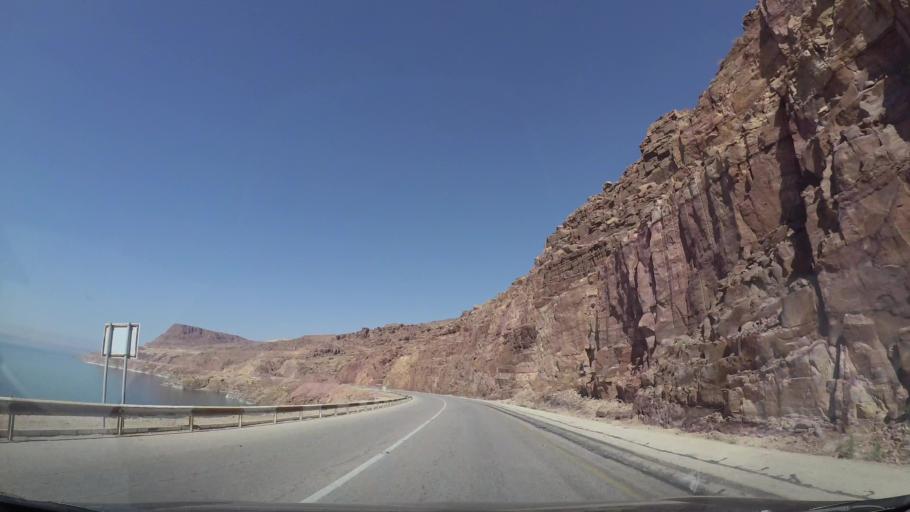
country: JO
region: Karak
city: Al Qasr
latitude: 31.4715
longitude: 35.5747
